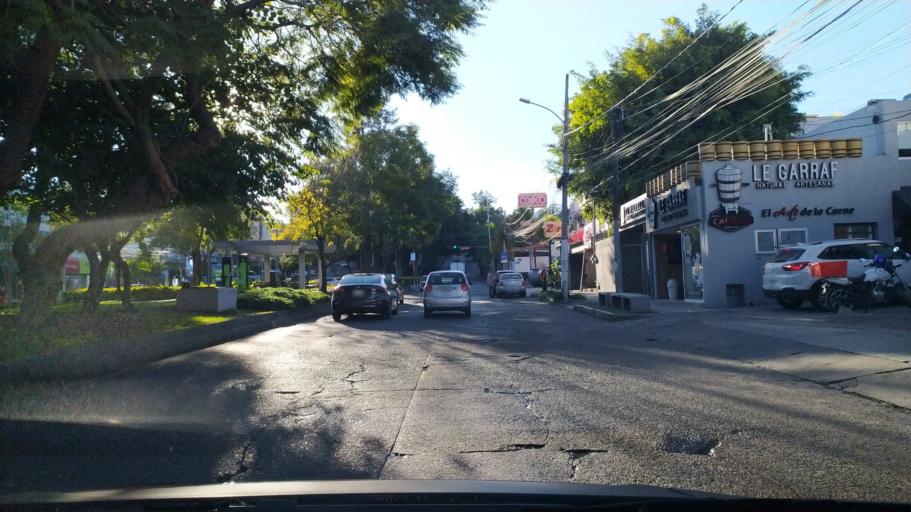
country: MX
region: Jalisco
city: Zapopan2
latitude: 20.6974
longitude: -103.3898
